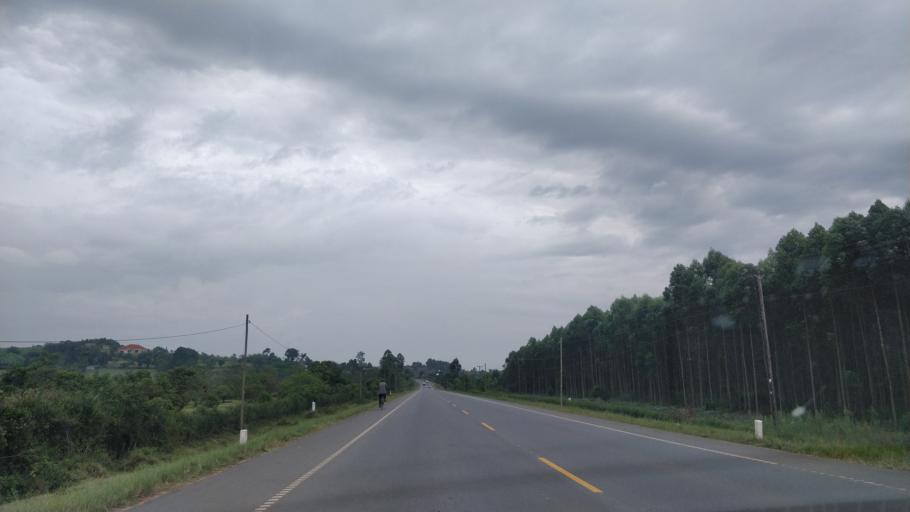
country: UG
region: Western Region
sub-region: Sheema District
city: Kibingo
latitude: -0.6568
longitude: 30.4747
